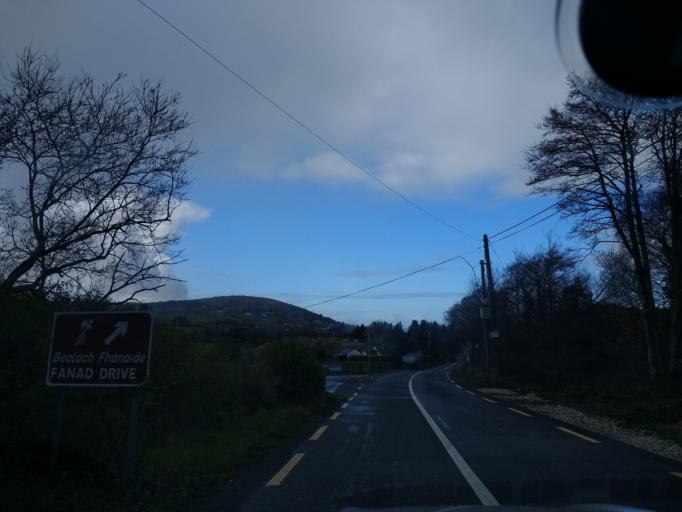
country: IE
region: Ulster
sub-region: County Donegal
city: Buncrana
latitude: 55.1339
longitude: -7.5323
